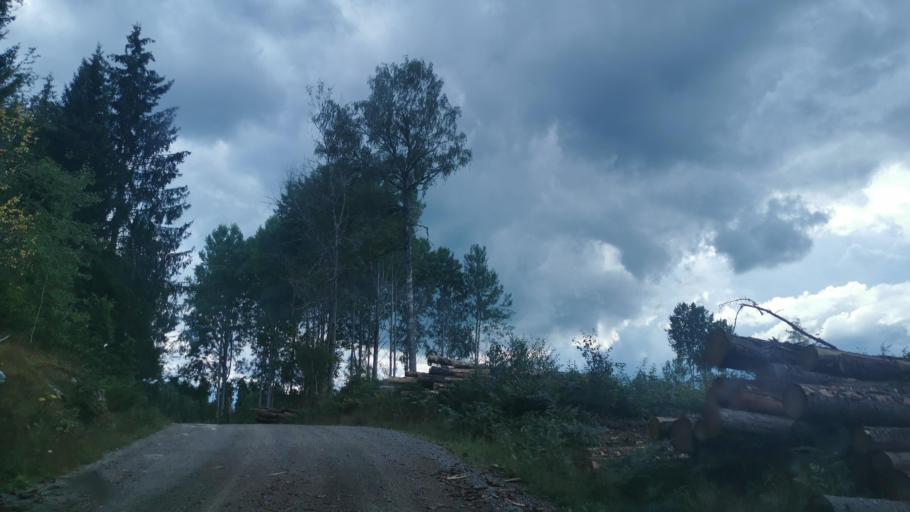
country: SE
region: OEstergoetland
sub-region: Finspangs Kommun
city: Finspang
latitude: 58.7882
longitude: 15.7674
